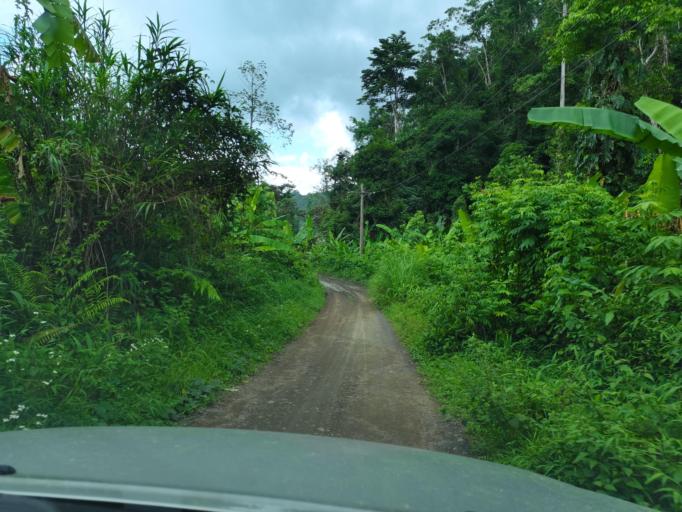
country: LA
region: Loungnamtha
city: Muang Long
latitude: 20.7741
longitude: 101.0168
